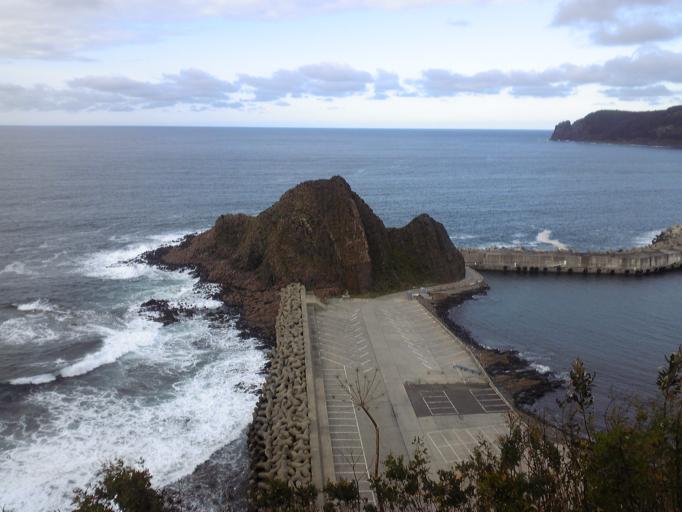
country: JP
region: Hokkaido
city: Shibetsu
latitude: 44.0732
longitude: 144.9903
